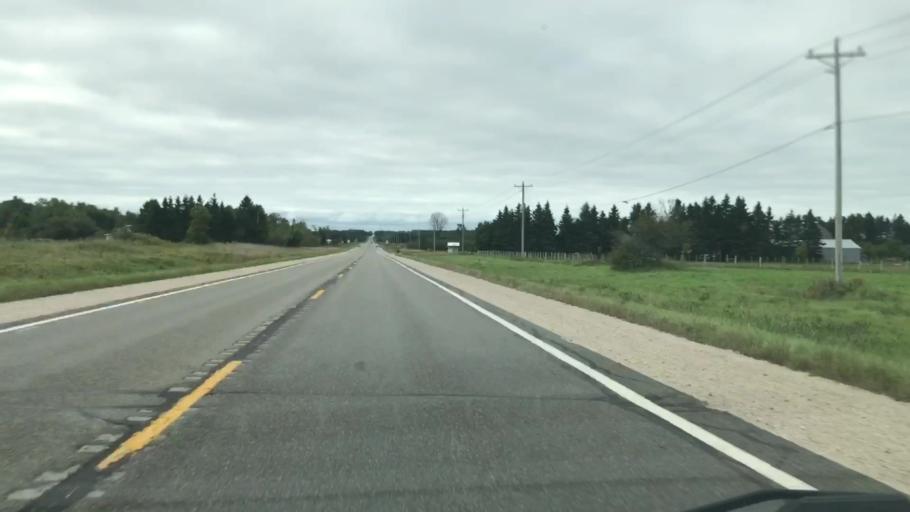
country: US
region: Michigan
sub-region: Luce County
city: Newberry
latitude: 46.1522
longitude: -85.5714
